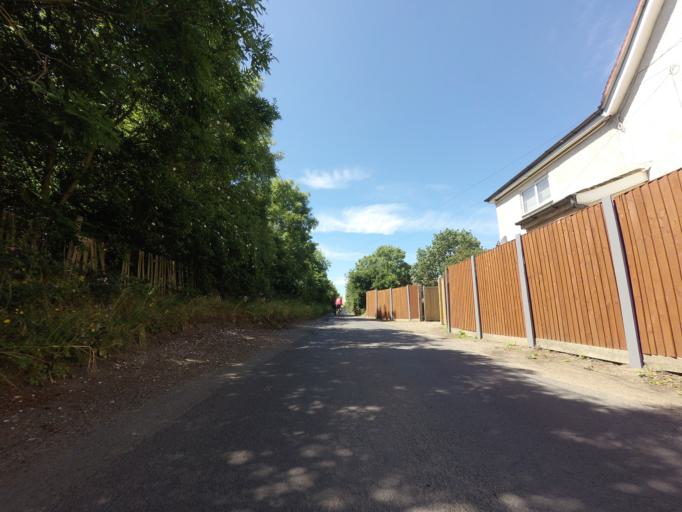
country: GB
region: England
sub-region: Kent
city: Strood
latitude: 51.4162
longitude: 0.5102
